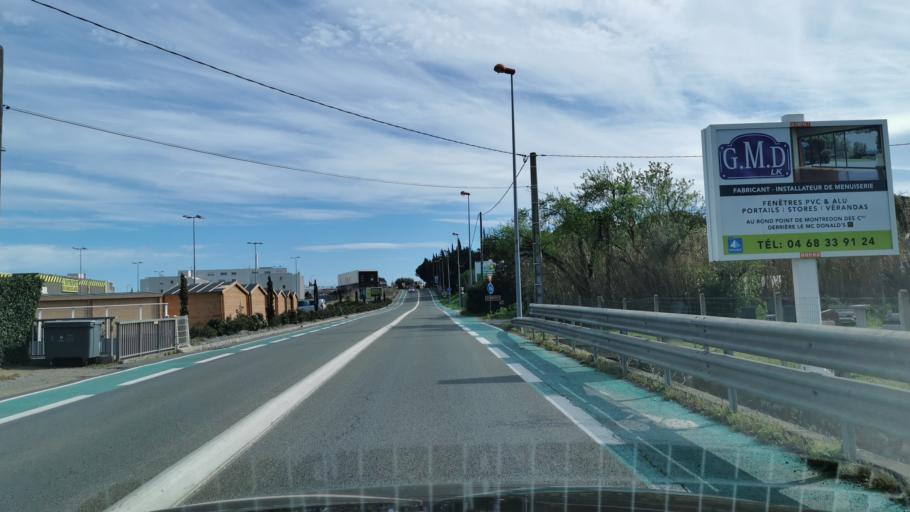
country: FR
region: Languedoc-Roussillon
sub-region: Departement de l'Aude
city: Narbonne
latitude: 43.1922
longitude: 2.9820
